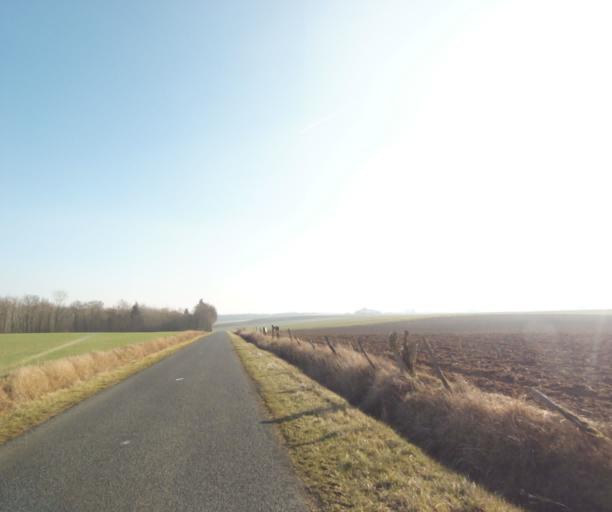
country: FR
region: Champagne-Ardenne
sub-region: Departement de la Haute-Marne
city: Chevillon
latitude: 48.4868
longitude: 5.0824
